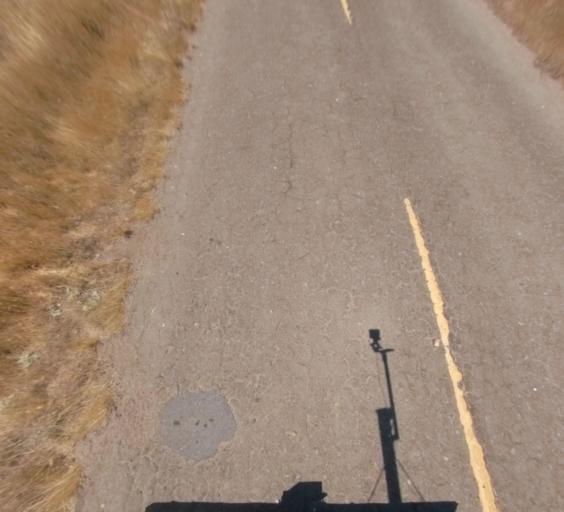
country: US
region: California
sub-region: Madera County
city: Madera Acres
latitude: 37.1011
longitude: -120.0007
